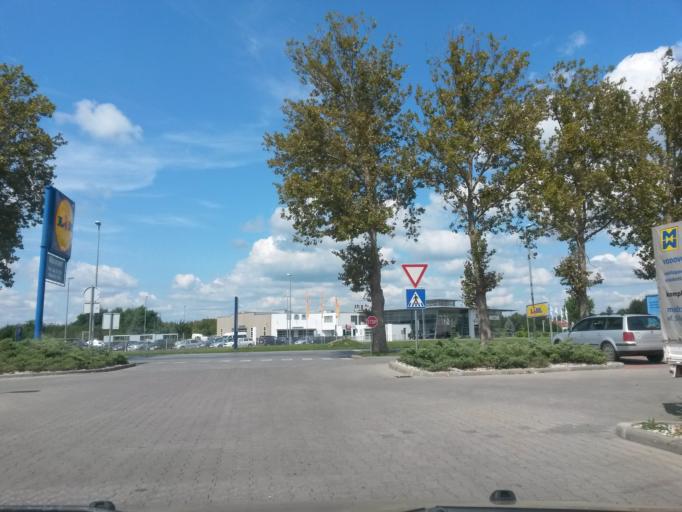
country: HR
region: Osjecko-Baranjska
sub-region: Grad Osijek
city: Osijek
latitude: 45.5496
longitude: 18.6675
